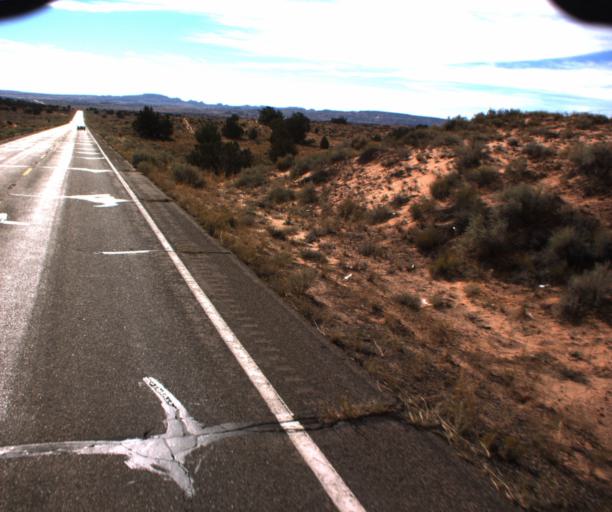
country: US
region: Arizona
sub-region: Coconino County
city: Kaibito
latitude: 36.6379
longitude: -111.2150
